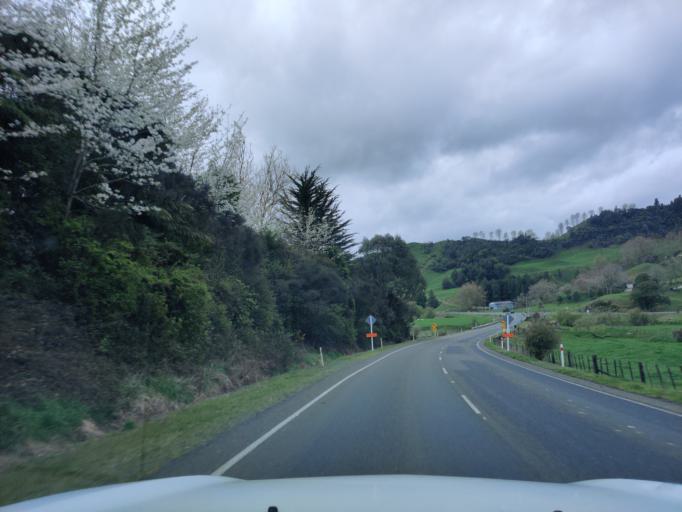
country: NZ
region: Waikato
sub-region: Otorohanga District
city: Otorohanga
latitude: -38.4902
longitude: 175.1872
